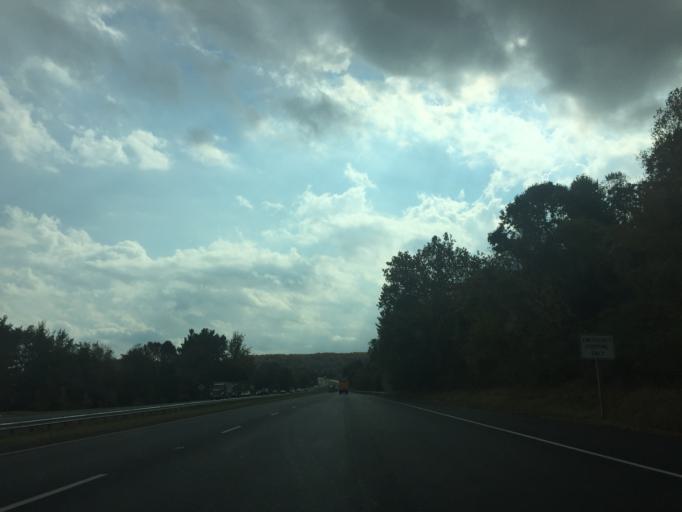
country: US
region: Maryland
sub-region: Baltimore County
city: Hunt Valley
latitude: 39.5478
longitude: -76.6669
